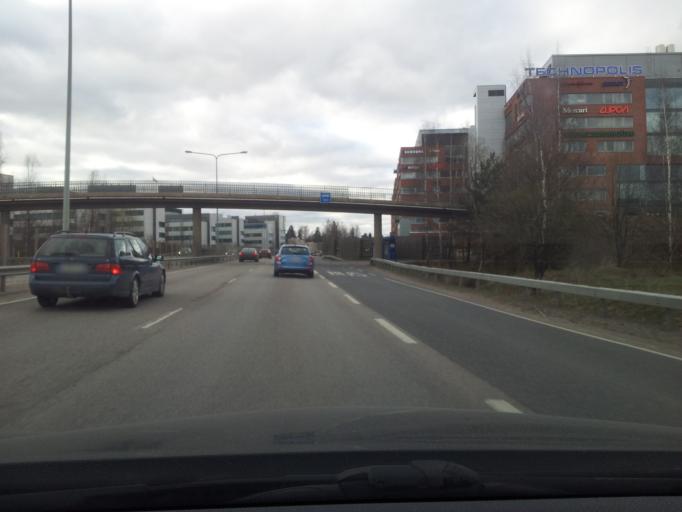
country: FI
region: Uusimaa
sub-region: Helsinki
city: Otaniemi
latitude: 60.1865
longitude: 24.8095
